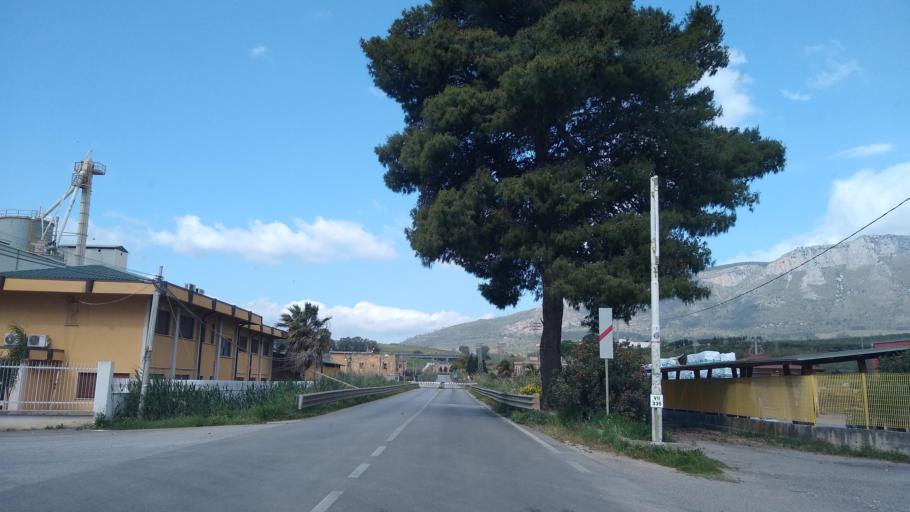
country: IT
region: Sicily
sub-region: Trapani
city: Alcamo
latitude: 37.9678
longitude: 12.9160
